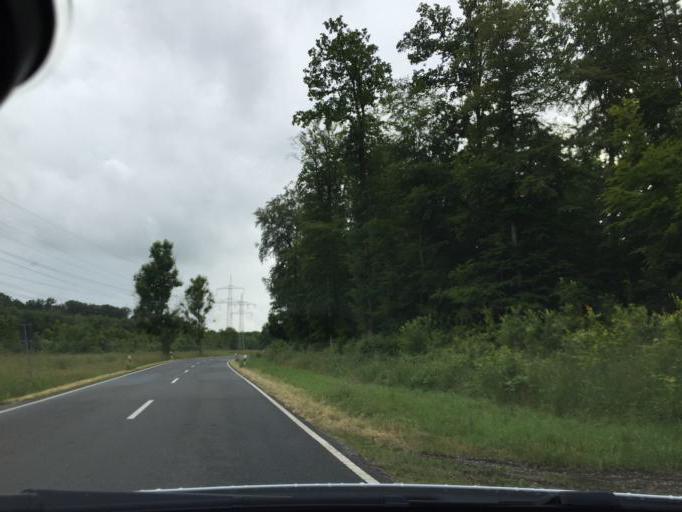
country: DE
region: Lower Saxony
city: Ottenstein
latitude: 52.0049
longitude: 9.3908
